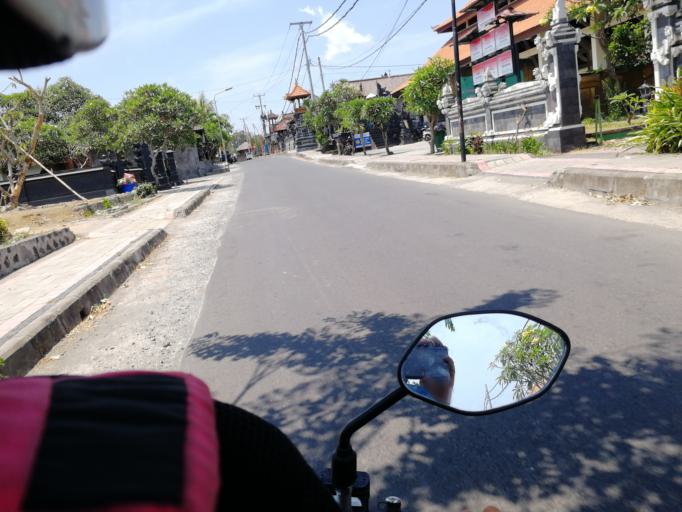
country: ID
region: Bali
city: Banjar Timbrah
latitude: -8.4791
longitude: 115.5974
